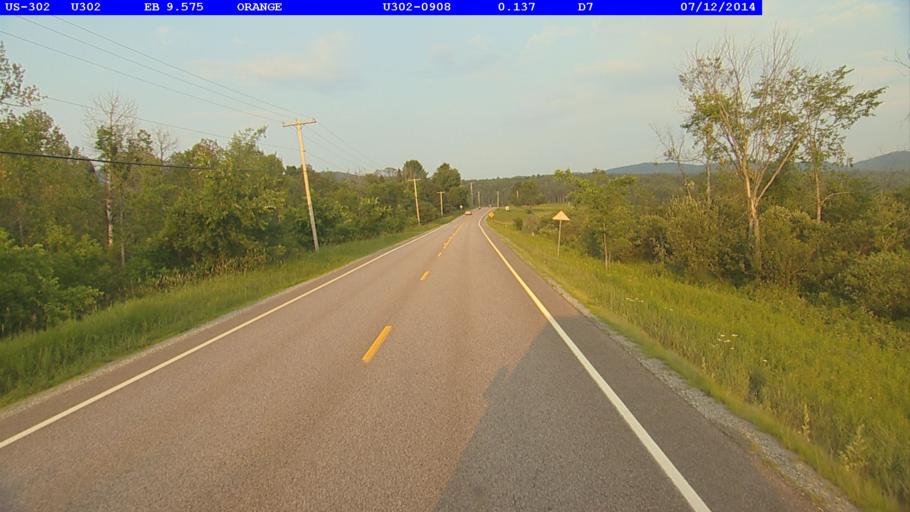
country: US
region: Vermont
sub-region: Washington County
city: South Barre
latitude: 44.1532
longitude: -72.4340
